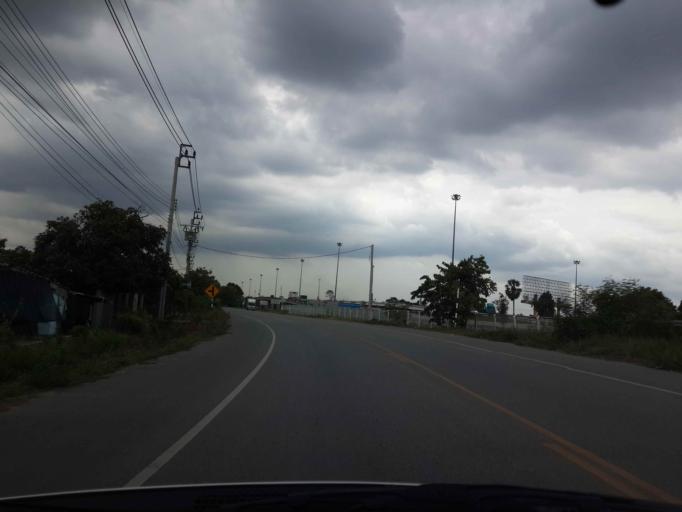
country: TH
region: Bangkok
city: Sai Mai
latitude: 13.8972
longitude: 100.6938
